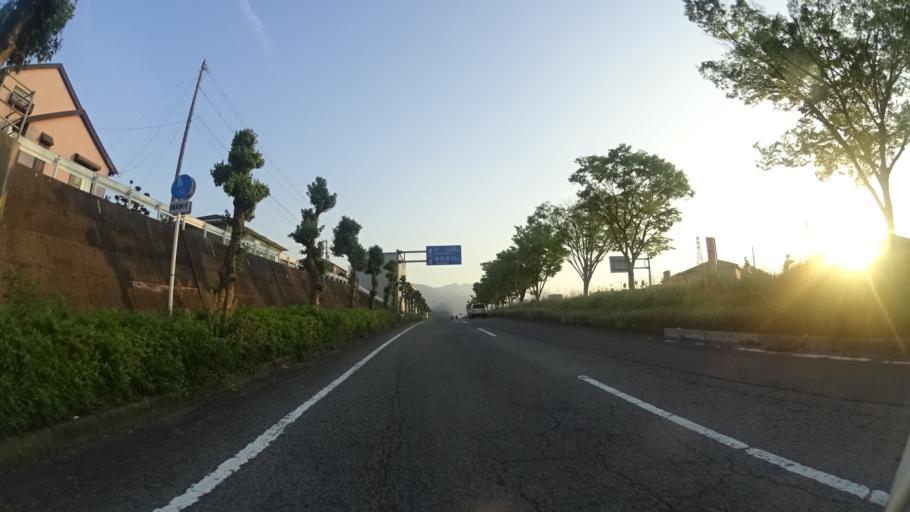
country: JP
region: Ehime
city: Kawanoecho
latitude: 33.9900
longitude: 133.5805
